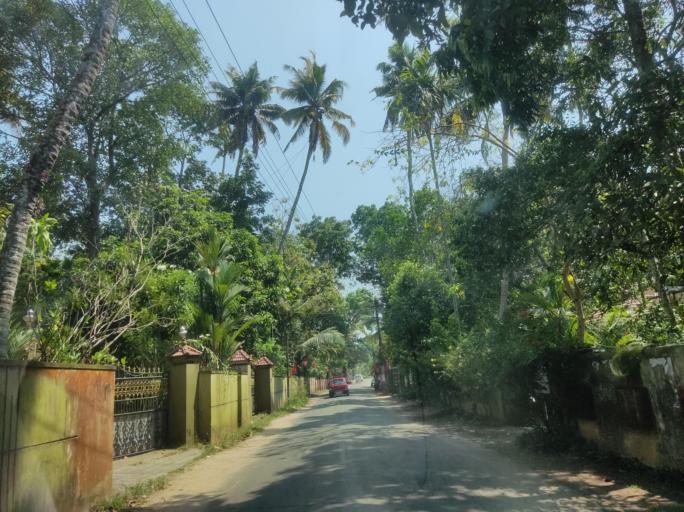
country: IN
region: Kerala
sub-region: Alappuzha
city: Vayalar
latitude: 9.6873
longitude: 76.3040
